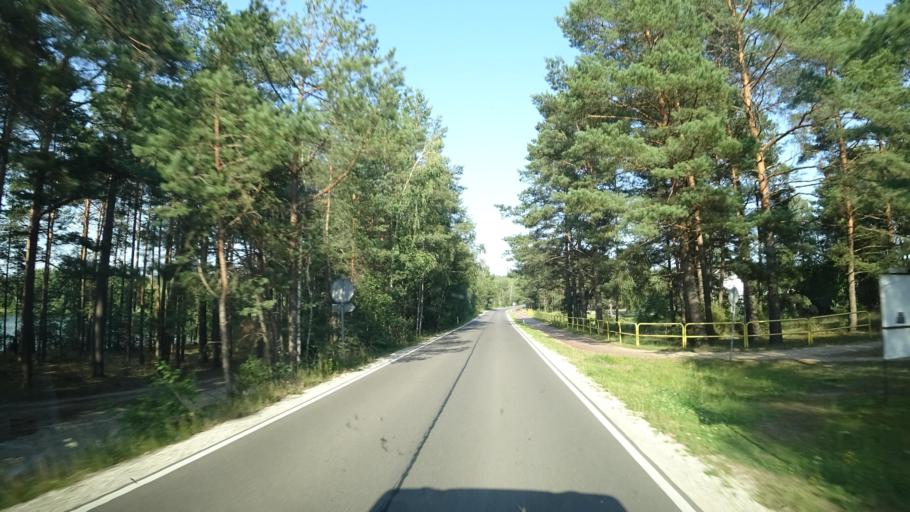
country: PL
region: Pomeranian Voivodeship
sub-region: Powiat bytowski
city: Lipnica
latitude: 53.8636
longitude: 17.5120
